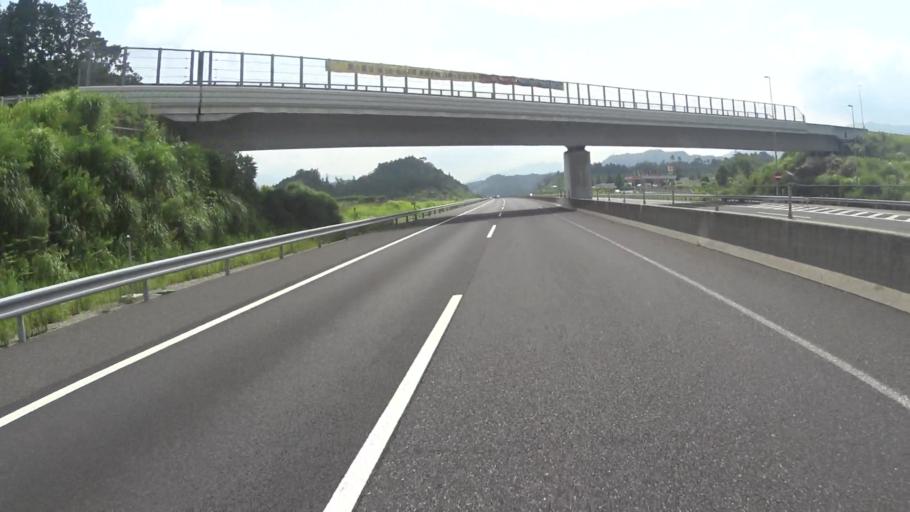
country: JP
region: Shiga Prefecture
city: Hino
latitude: 34.9165
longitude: 136.2891
